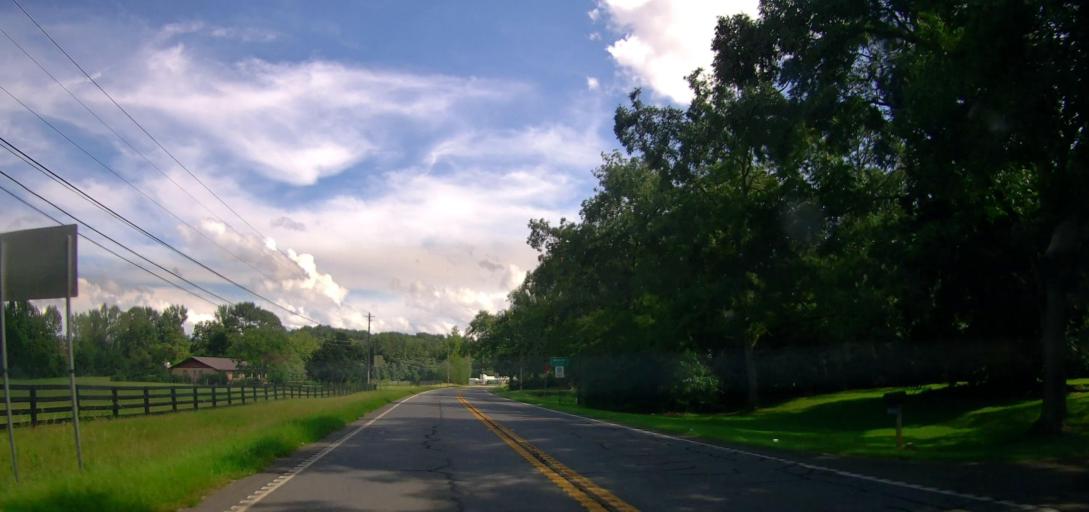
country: US
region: Georgia
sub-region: Talbot County
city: Sardis
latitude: 32.7939
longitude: -84.5666
